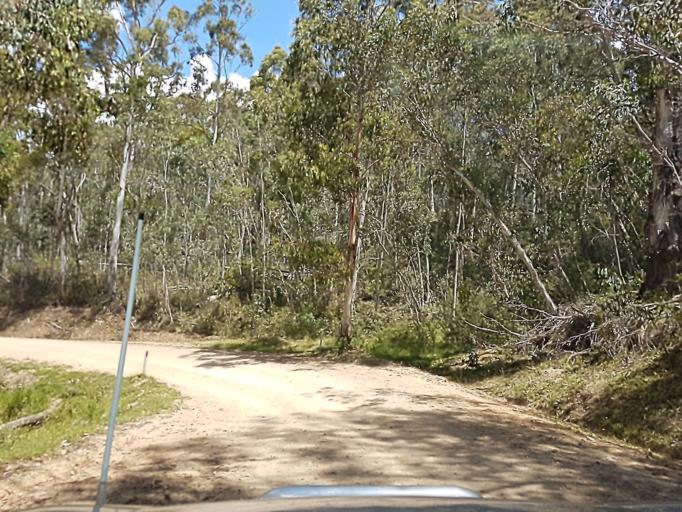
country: AU
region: New South Wales
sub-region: Snowy River
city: Jindabyne
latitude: -36.8850
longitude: 148.0840
